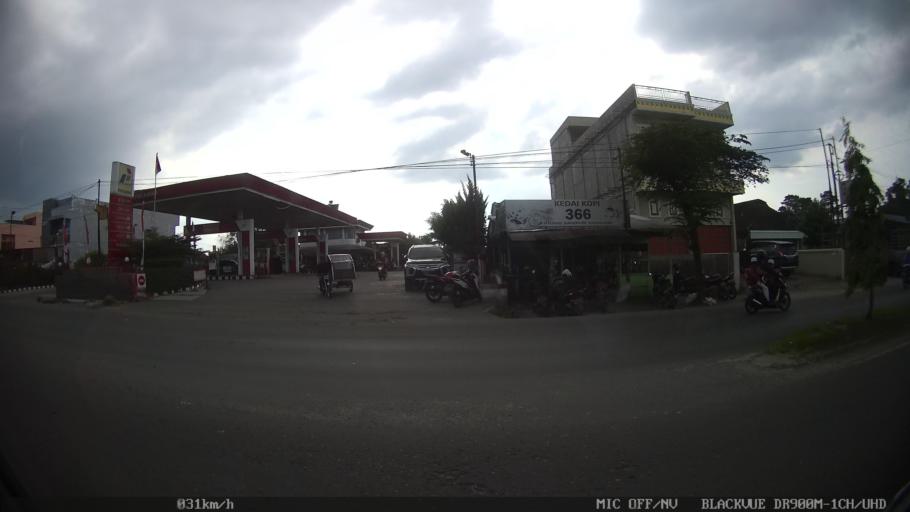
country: ID
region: North Sumatra
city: Sunggal
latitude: 3.5388
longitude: 98.6223
